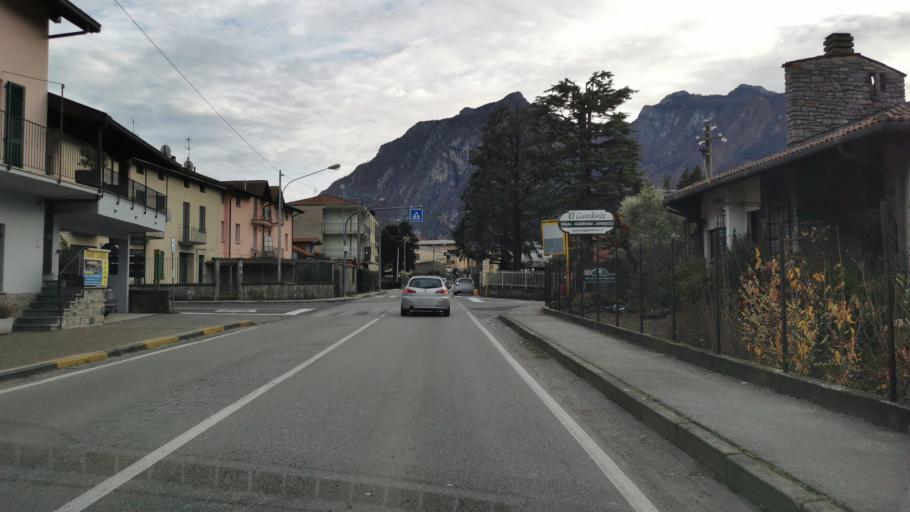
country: IT
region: Lombardy
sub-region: Provincia di Lecco
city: Abbadia Lariana
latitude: 45.9031
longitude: 9.3317
